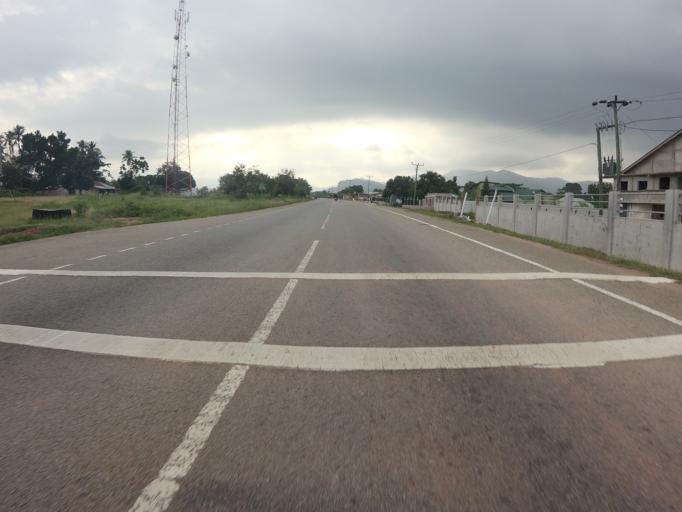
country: GH
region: Volta
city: Ho
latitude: 6.7733
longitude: 0.4788
